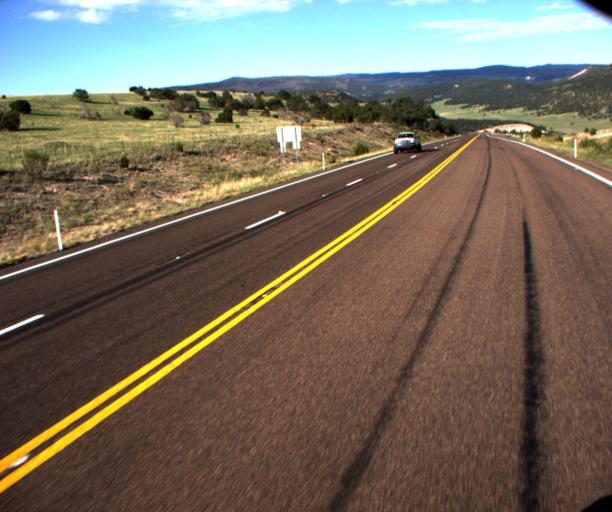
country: US
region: Arizona
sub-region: Apache County
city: Eagar
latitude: 34.0948
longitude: -109.2292
